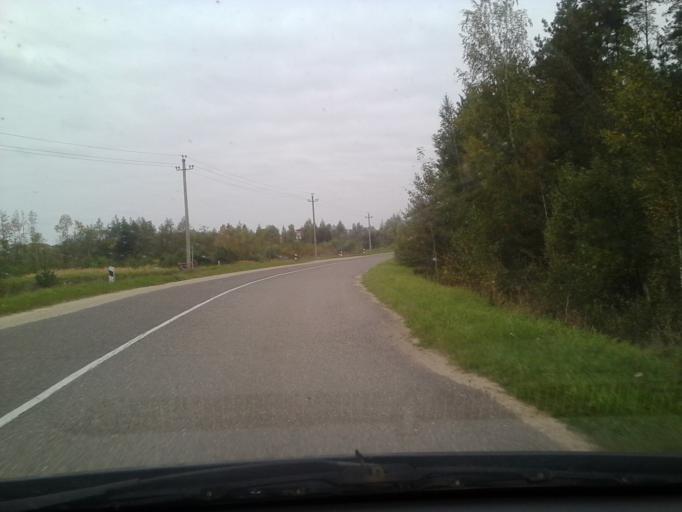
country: BY
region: Vitebsk
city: Pastavy
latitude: 55.0861
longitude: 26.8383
